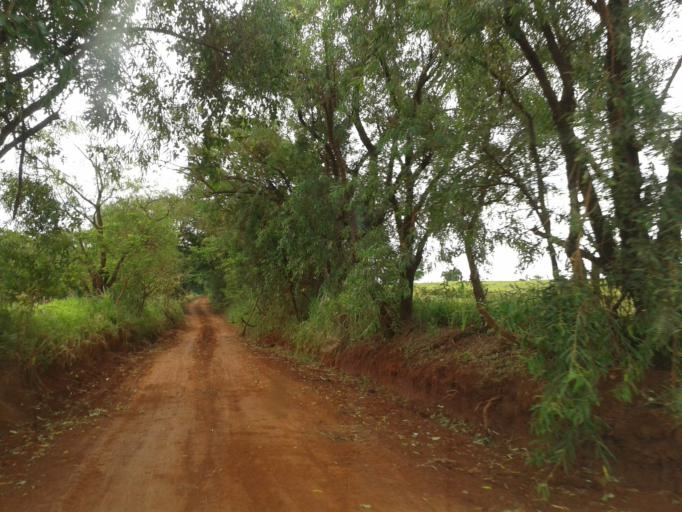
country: BR
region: Minas Gerais
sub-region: Centralina
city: Centralina
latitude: -18.6507
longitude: -49.3382
